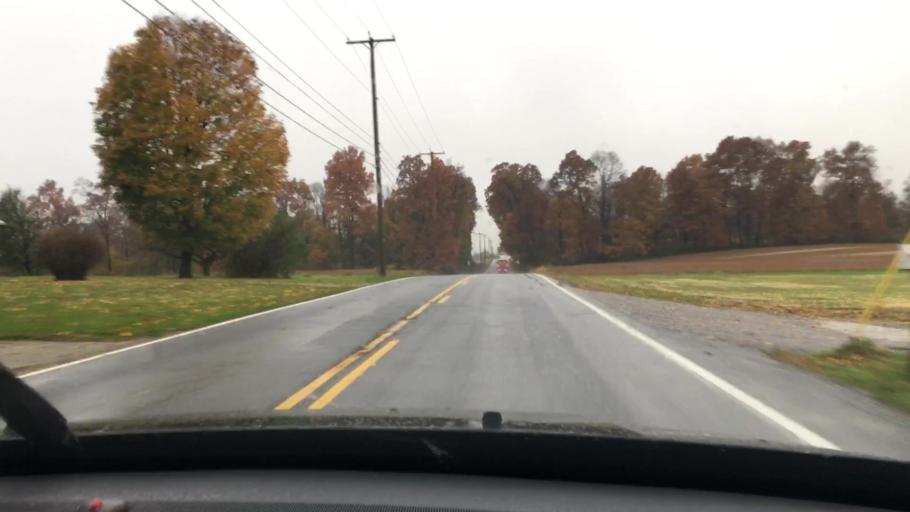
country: US
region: Pennsylvania
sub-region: York County
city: Stewartstown
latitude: 39.7238
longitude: -76.5316
